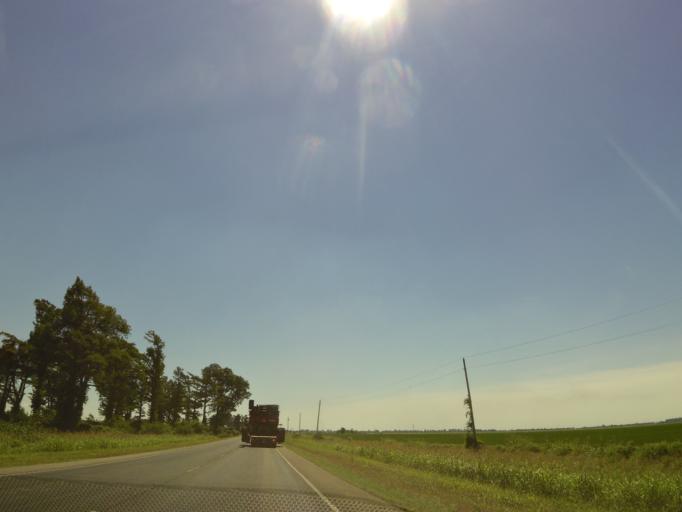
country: US
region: Missouri
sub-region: New Madrid County
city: Lilbourn
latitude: 36.5539
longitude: -89.7183
